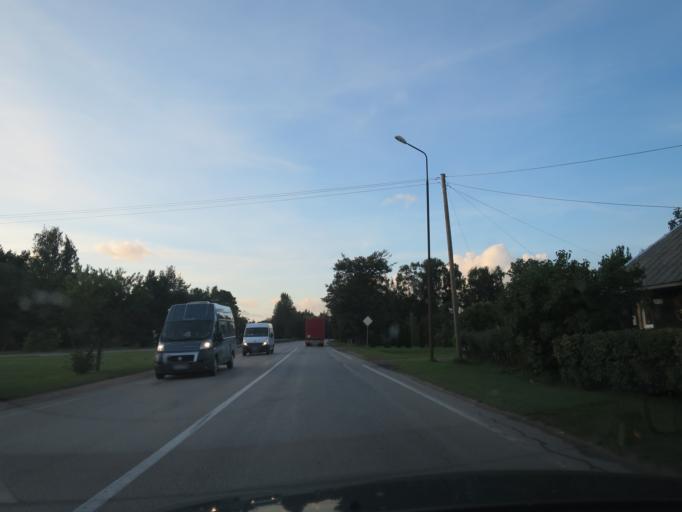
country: LV
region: Salacgrivas
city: Salacgriva
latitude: 57.7604
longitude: 24.3587
